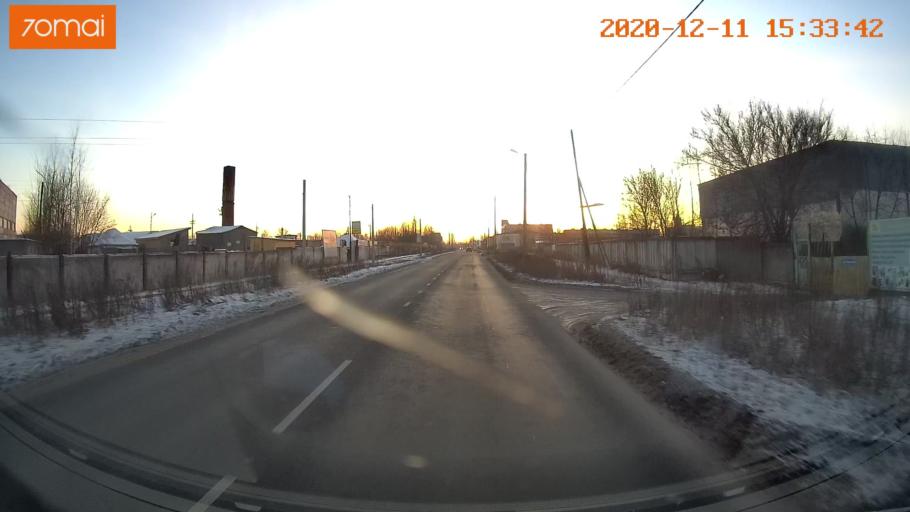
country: RU
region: Ivanovo
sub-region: Gorod Ivanovo
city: Ivanovo
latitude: 57.0501
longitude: 40.9452
